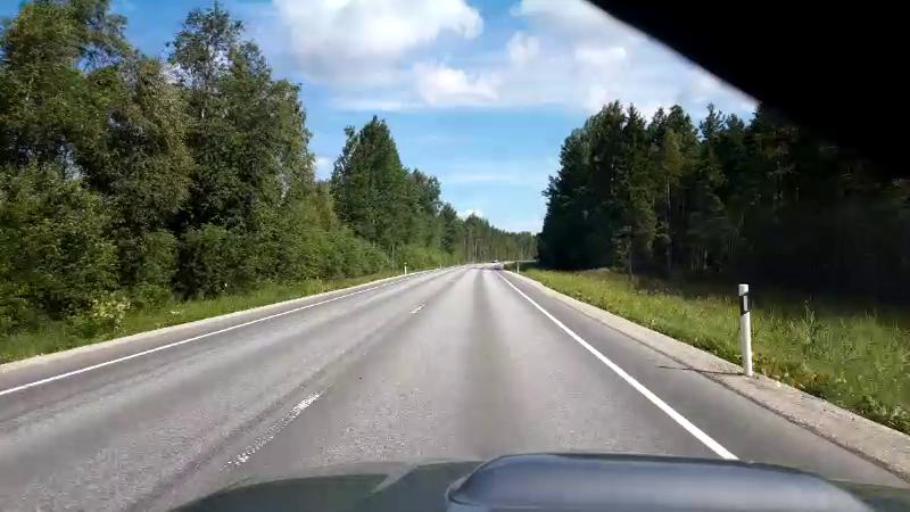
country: EE
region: Jaervamaa
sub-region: Paide linn
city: Paide
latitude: 58.9986
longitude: 25.6770
